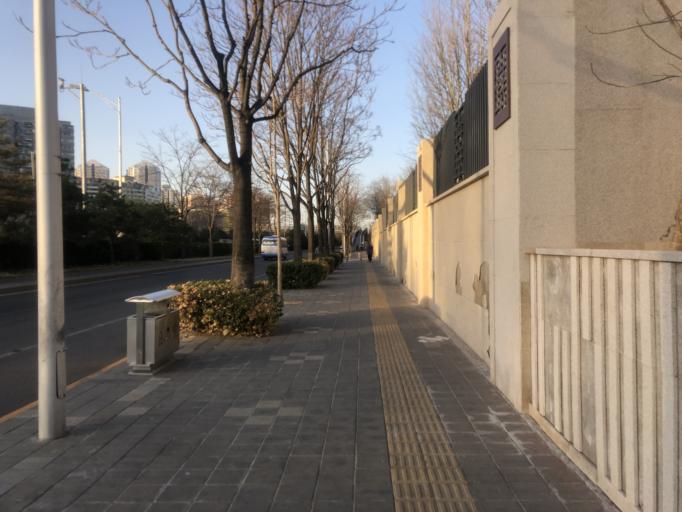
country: CN
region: Beijing
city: Datun
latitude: 39.9773
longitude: 116.4313
